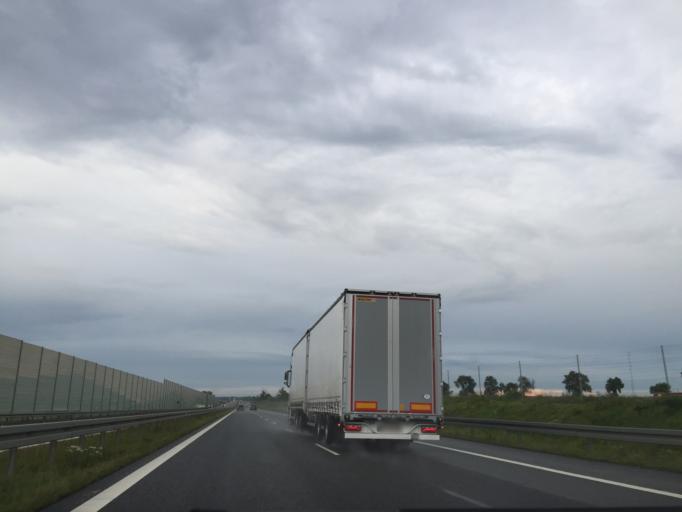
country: PL
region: Podlasie
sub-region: Powiat zambrowski
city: Zambrow
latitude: 53.0046
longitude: 22.2761
